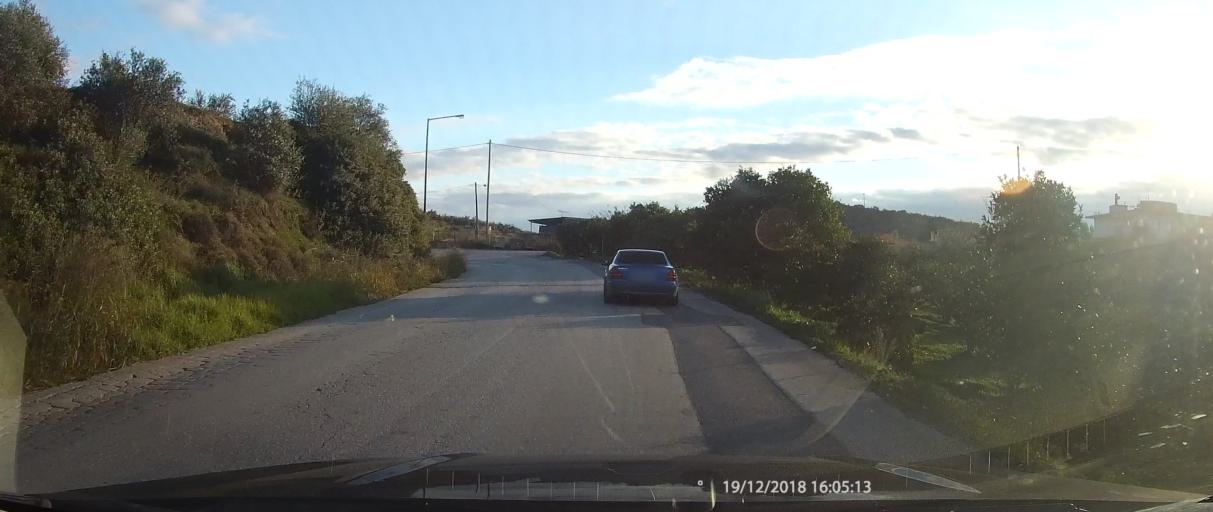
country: GR
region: Peloponnese
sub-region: Nomos Lakonias
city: Vlakhiotis
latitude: 36.8616
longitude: 22.7179
